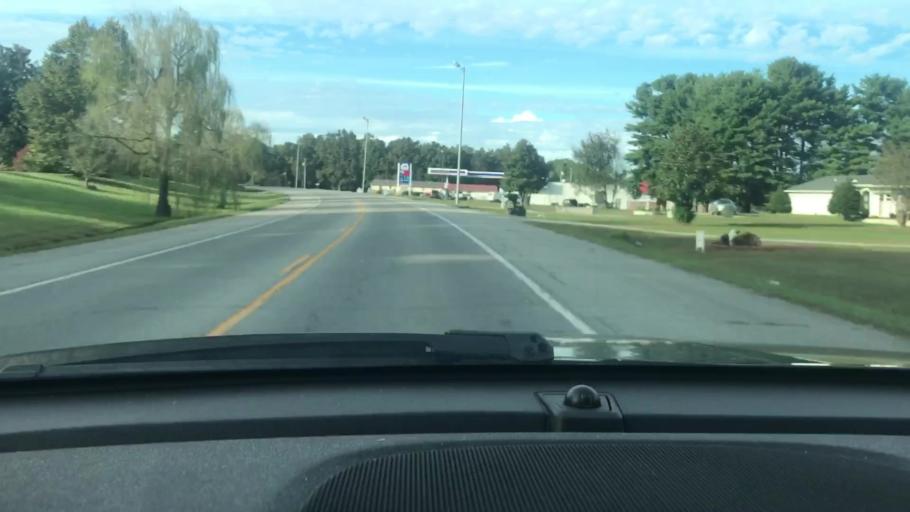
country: US
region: Tennessee
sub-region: Dickson County
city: White Bluff
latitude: 36.1249
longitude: -87.2272
